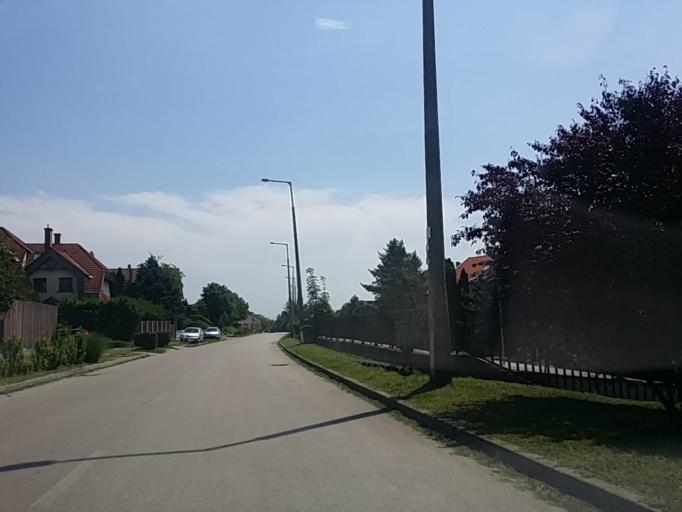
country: HU
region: Pest
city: Szentendre
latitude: 47.6702
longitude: 19.0548
